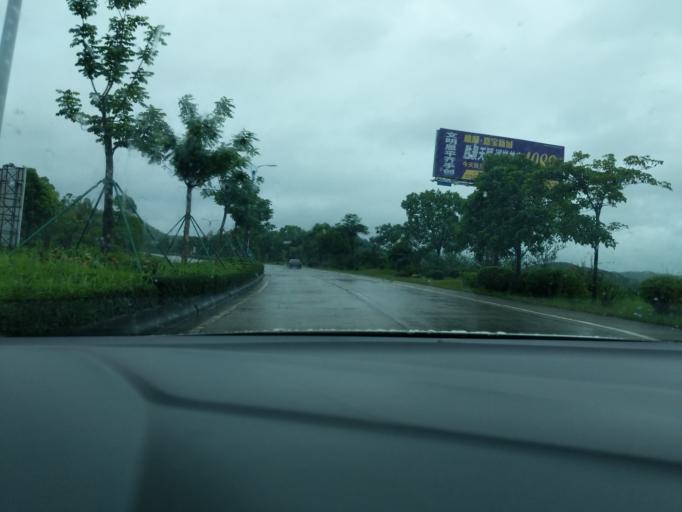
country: CN
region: Guangdong
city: Pingshi
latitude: 22.2247
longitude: 112.3162
